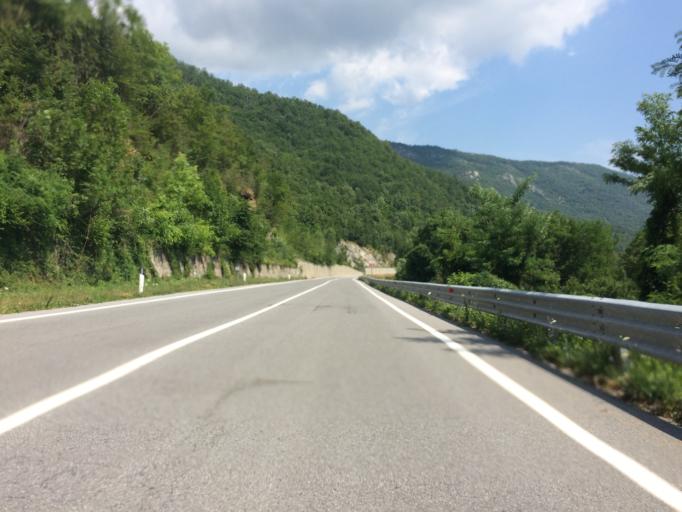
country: IT
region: Piedmont
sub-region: Provincia di Cuneo
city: Garessio
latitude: 44.1783
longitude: 7.9813
